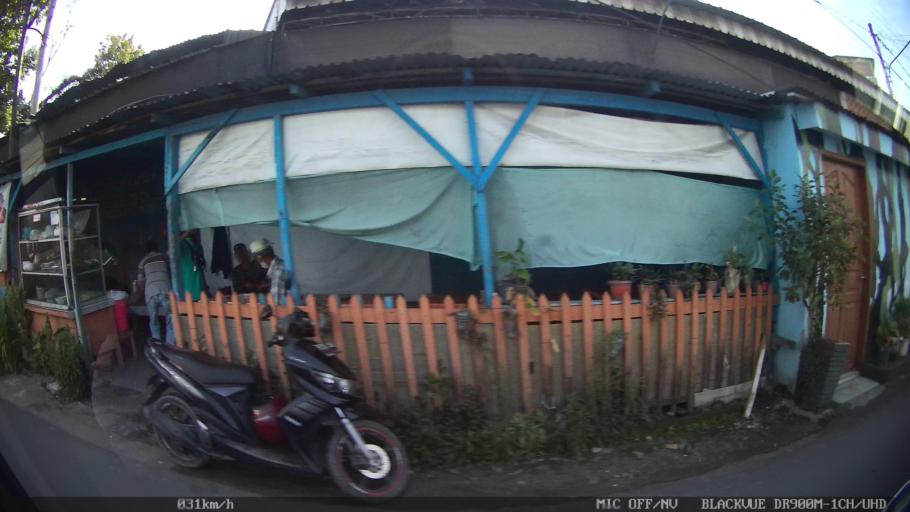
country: ID
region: North Sumatra
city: Medan
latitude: 3.5939
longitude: 98.6665
